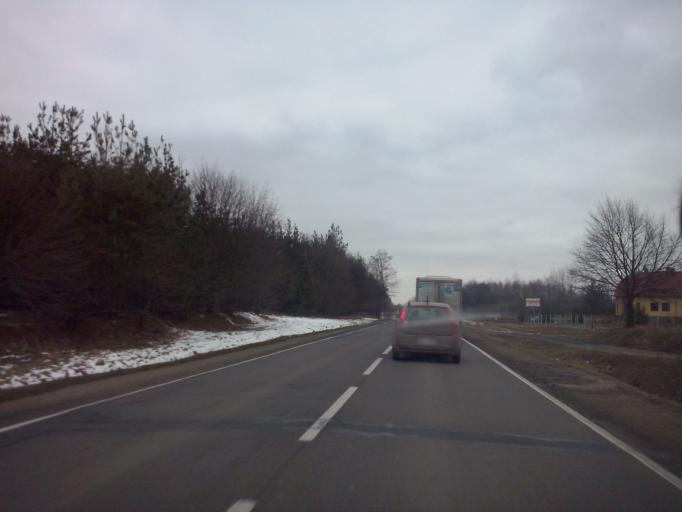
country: PL
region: Subcarpathian Voivodeship
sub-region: Powiat nizanski
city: Przedzel
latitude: 50.4867
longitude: 22.2211
